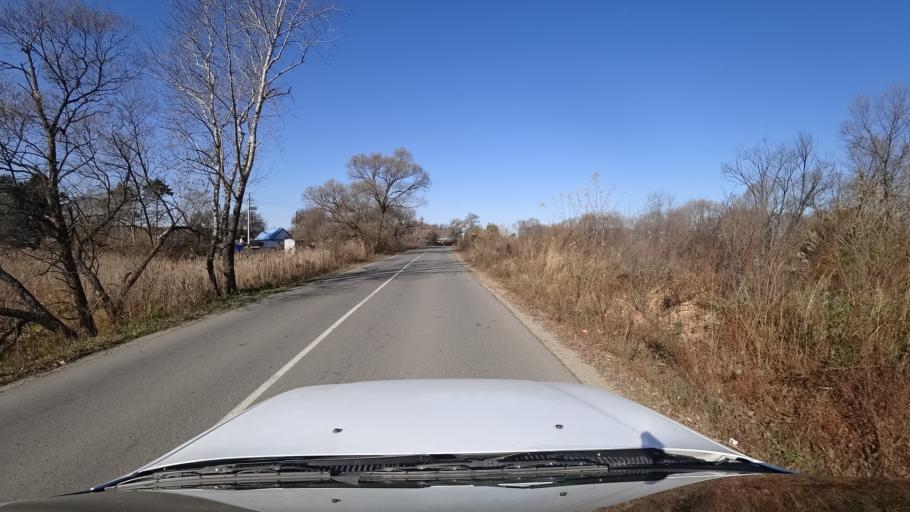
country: RU
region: Primorskiy
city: Dal'nerechensk
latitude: 45.9332
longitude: 133.7115
